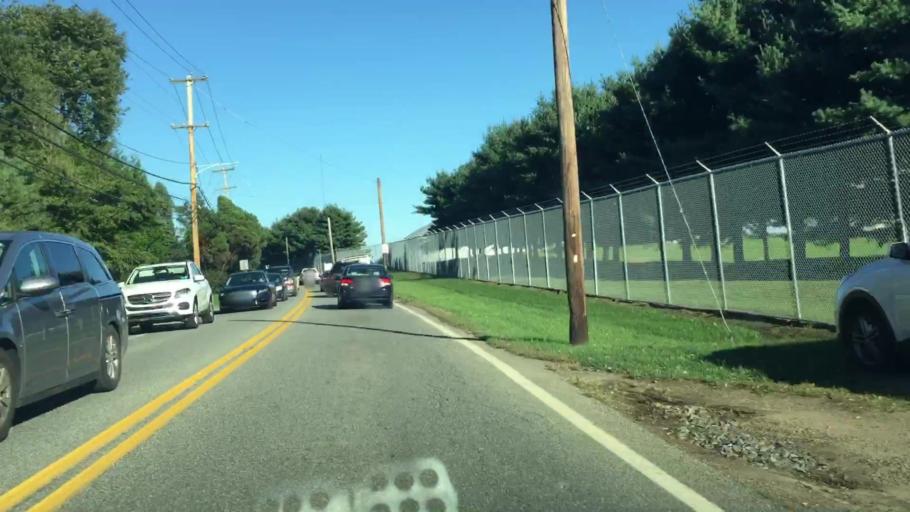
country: US
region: Pennsylvania
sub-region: Delaware County
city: Chester Heights
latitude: 39.8678
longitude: -75.4594
